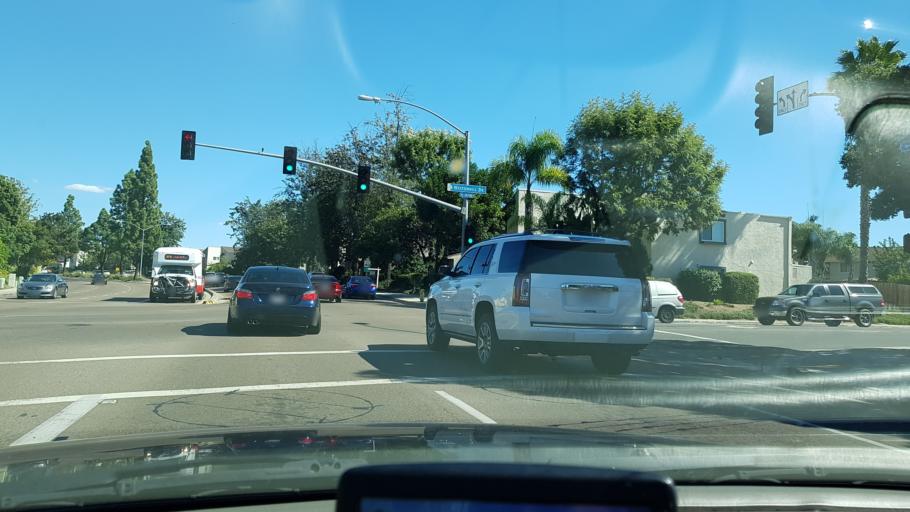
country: US
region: California
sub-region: San Diego County
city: Fairbanks Ranch
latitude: 32.9128
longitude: -117.1359
